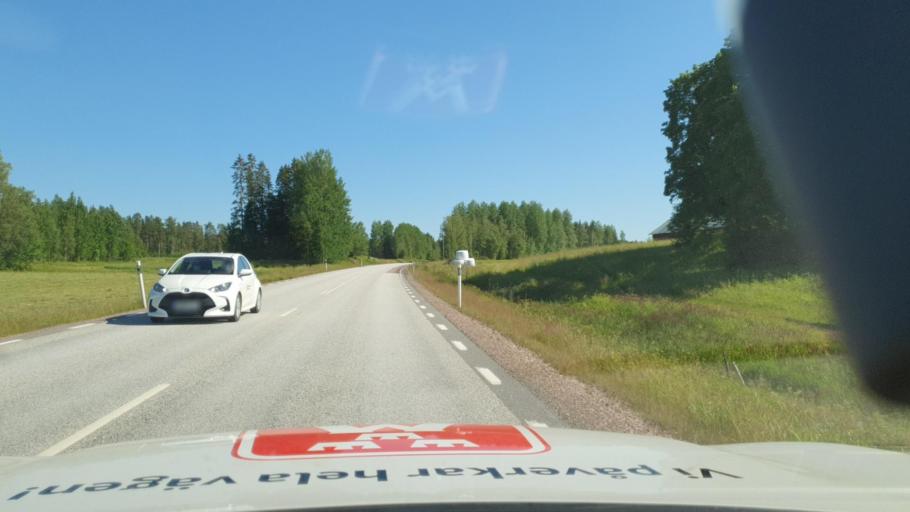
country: SE
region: Vaermland
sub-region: Storfors Kommun
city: Storfors
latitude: 59.4969
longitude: 14.3245
